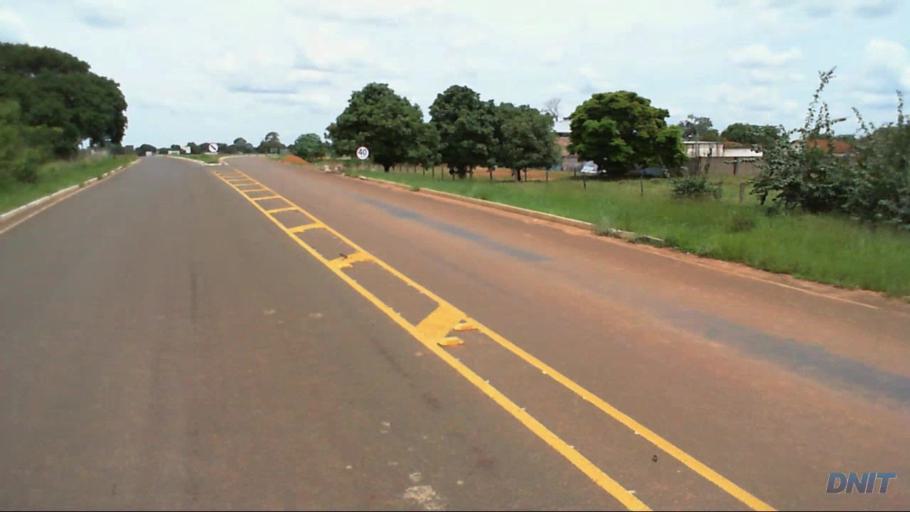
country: BR
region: Goias
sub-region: Sao Miguel Do Araguaia
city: Sao Miguel do Araguaia
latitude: -13.2847
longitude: -50.1872
